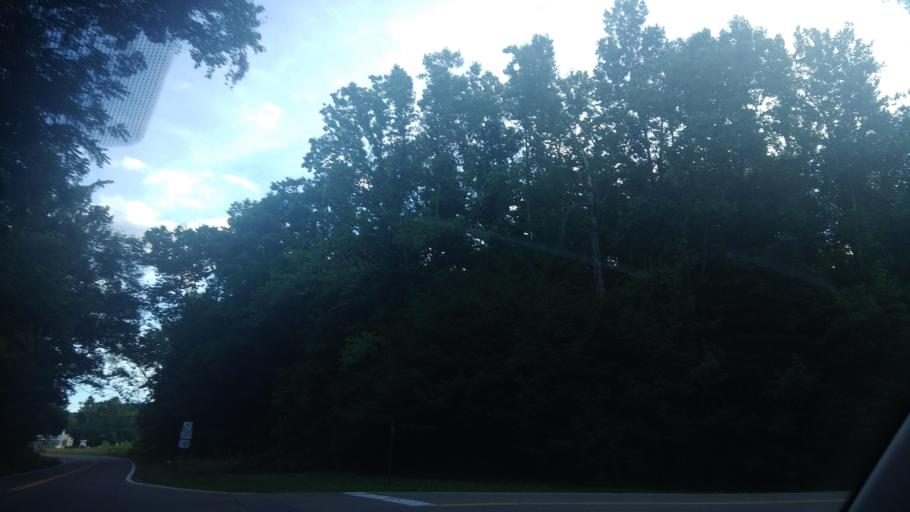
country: US
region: Tennessee
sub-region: Cocke County
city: Newport
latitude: 35.8132
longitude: -83.2474
